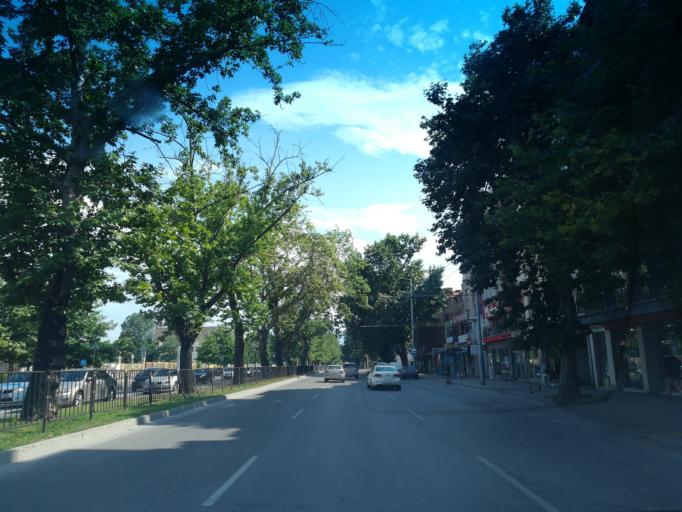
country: BG
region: Plovdiv
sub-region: Obshtina Plovdiv
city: Plovdiv
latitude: 42.1408
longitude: 24.7630
